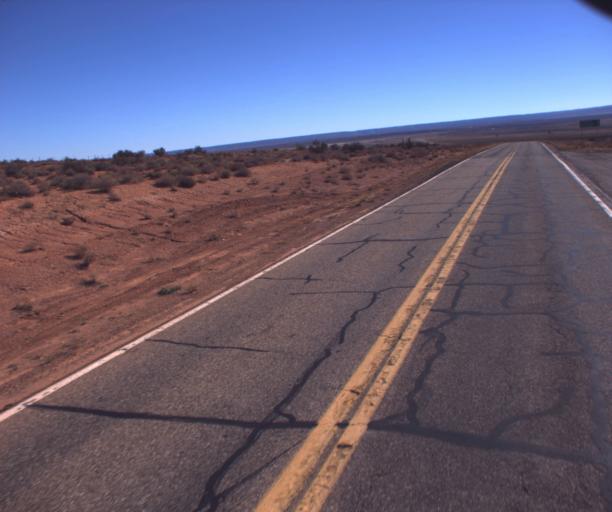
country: US
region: Arizona
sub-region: Coconino County
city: Fredonia
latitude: 36.9305
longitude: -112.4926
